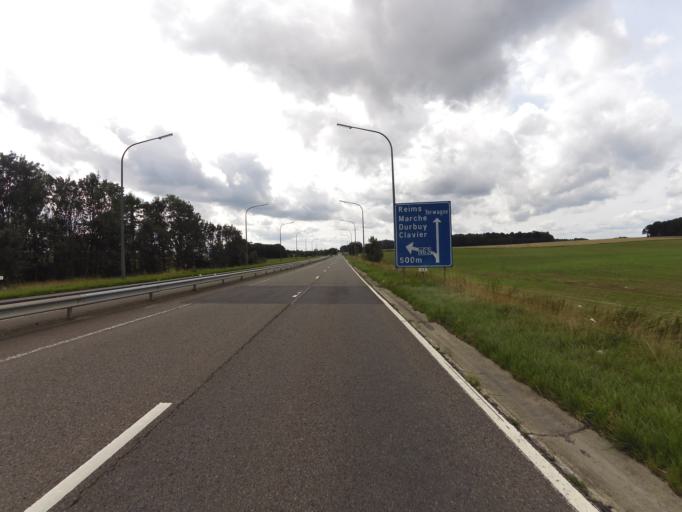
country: BE
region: Wallonia
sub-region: Province de Liege
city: Tinlot
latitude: 50.4586
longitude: 5.3613
